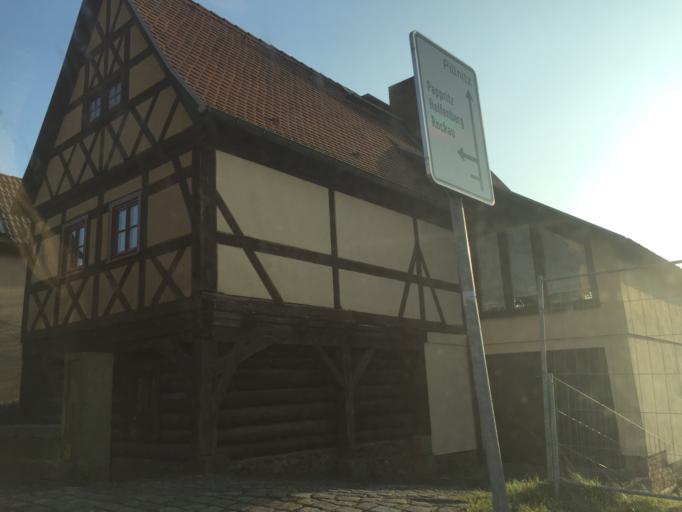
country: DE
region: Saxony
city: Heidenau
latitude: 51.0291
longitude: 13.8458
